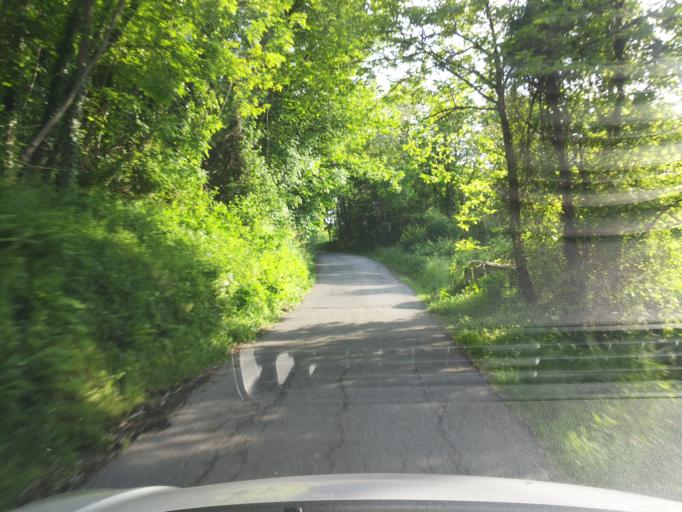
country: IT
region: Piedmont
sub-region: Provincia di Torino
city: Cossano Canavese
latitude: 45.3929
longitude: 8.0048
